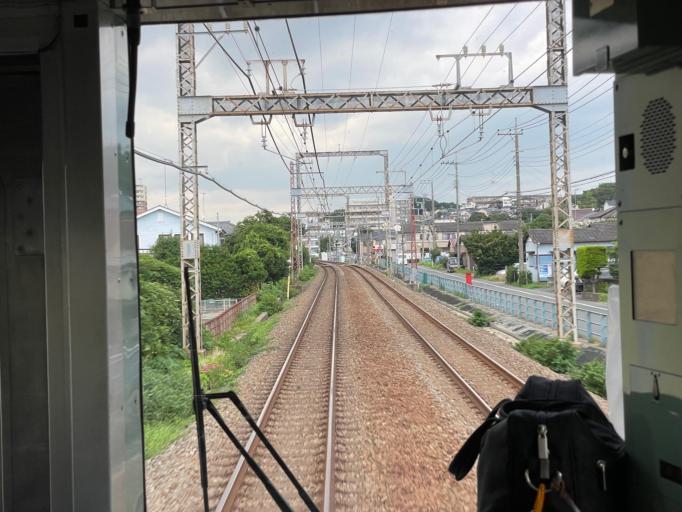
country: JP
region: Kanagawa
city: Zama
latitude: 35.4754
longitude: 139.3999
